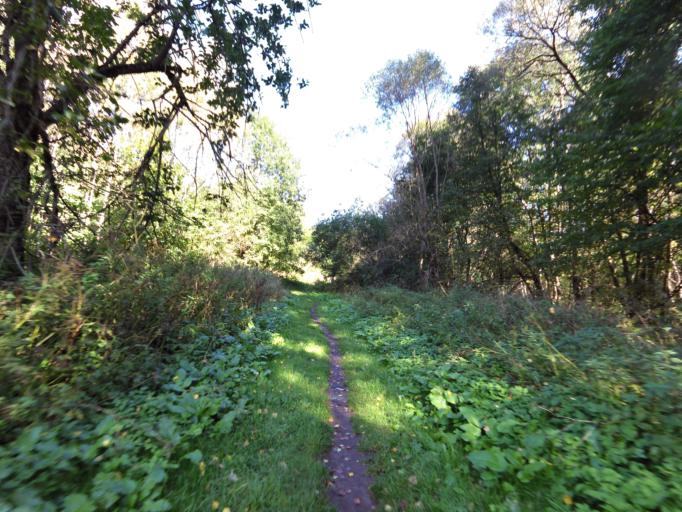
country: LT
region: Vilnius County
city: Pilaite
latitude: 54.7010
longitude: 25.1893
